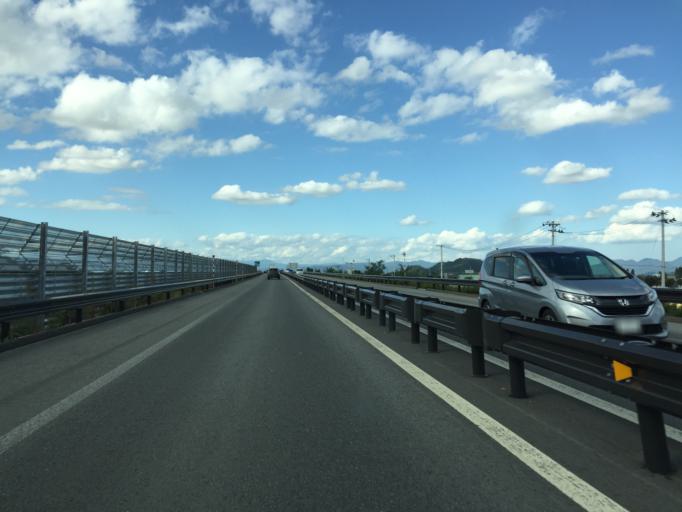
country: JP
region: Yamagata
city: Yonezawa
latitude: 37.9061
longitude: 140.1428
